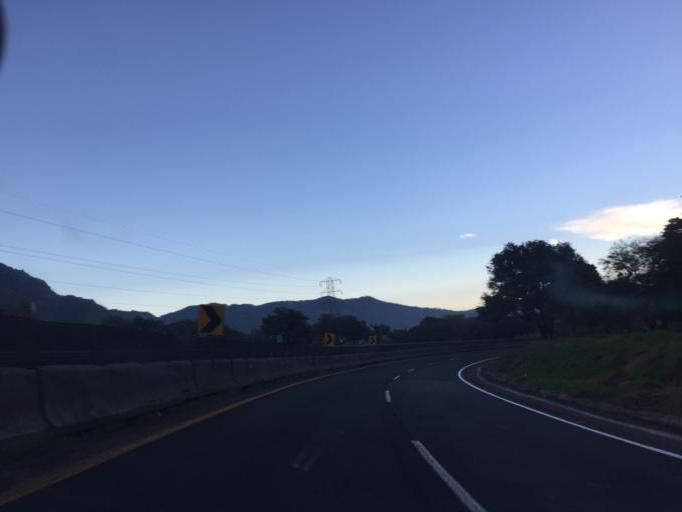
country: MX
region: Veracruz
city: Nogales
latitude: 18.8295
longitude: -97.1497
